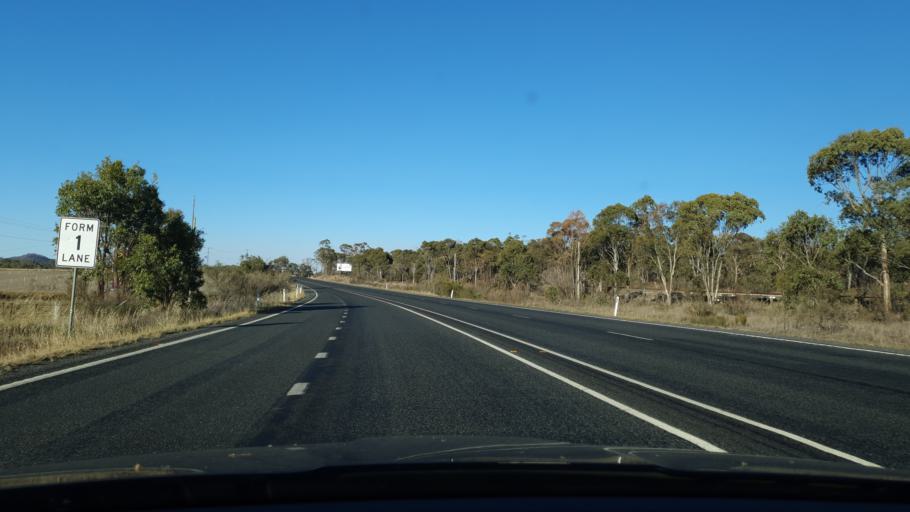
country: AU
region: Queensland
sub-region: Southern Downs
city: Stanthorpe
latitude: -28.6890
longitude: 151.9106
